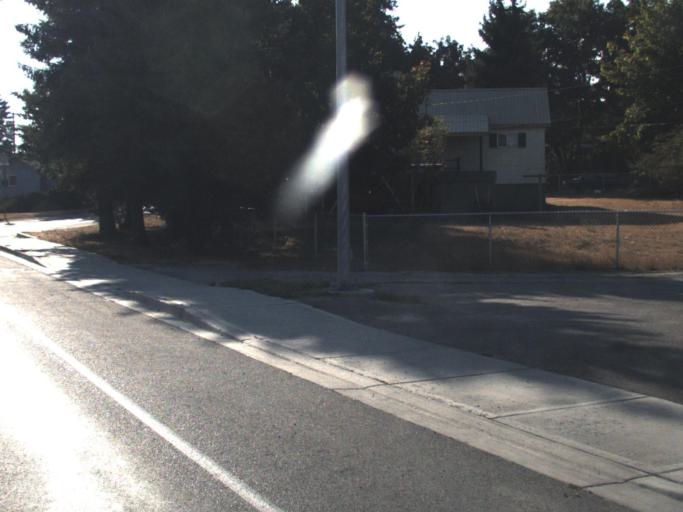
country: US
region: Washington
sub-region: Pend Oreille County
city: Newport
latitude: 48.1772
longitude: -117.0461
